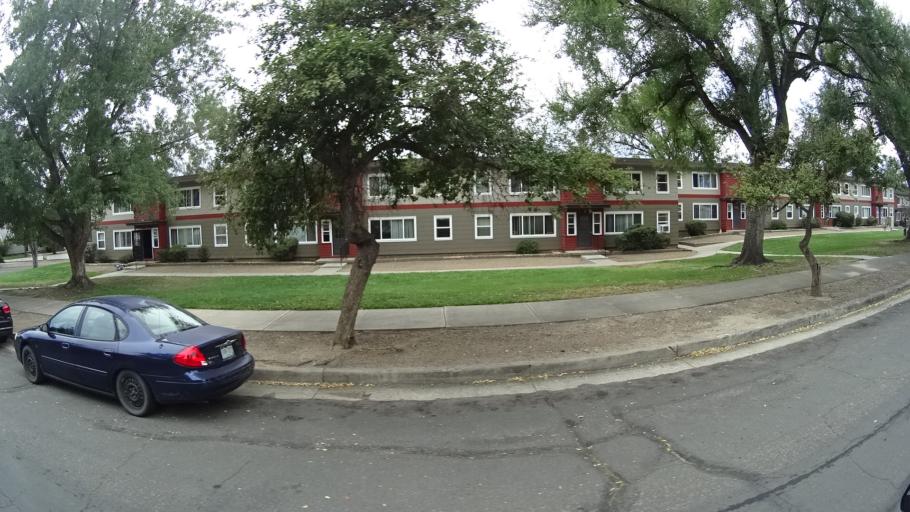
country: US
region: Colorado
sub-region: El Paso County
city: Colorado Springs
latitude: 38.8658
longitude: -104.7898
